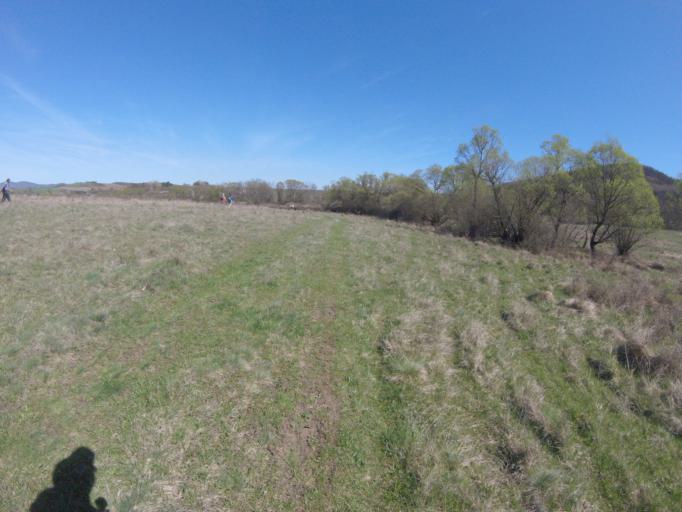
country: HU
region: Borsod-Abauj-Zemplen
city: Szendro
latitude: 48.4108
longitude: 20.7763
